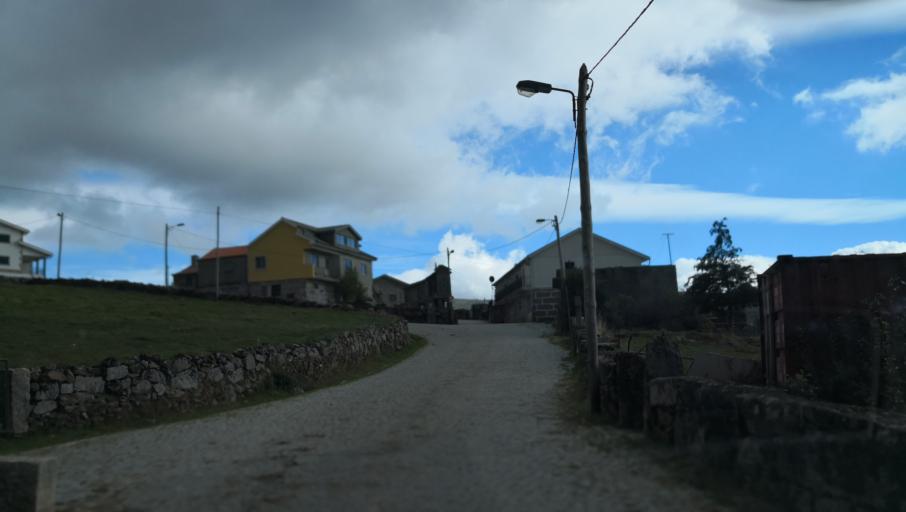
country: PT
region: Vila Real
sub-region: Vila Real
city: Vila Real
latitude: 41.3707
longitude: -7.7979
